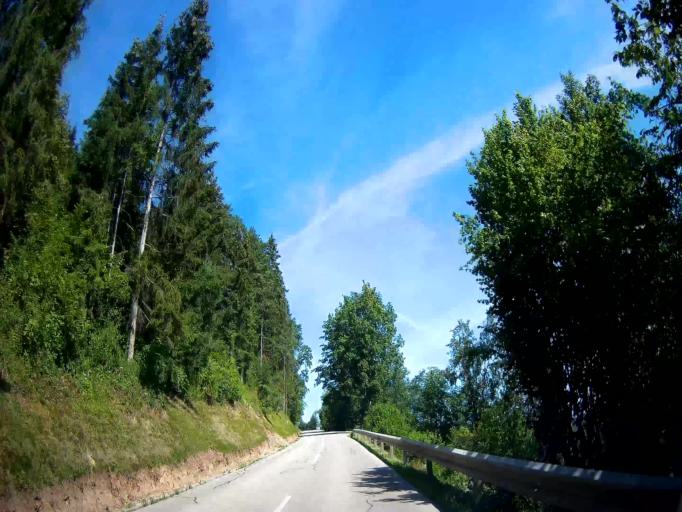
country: AT
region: Carinthia
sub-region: Politischer Bezirk Sankt Veit an der Glan
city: St. Georgen am Laengsee
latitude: 46.7875
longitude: 14.4192
